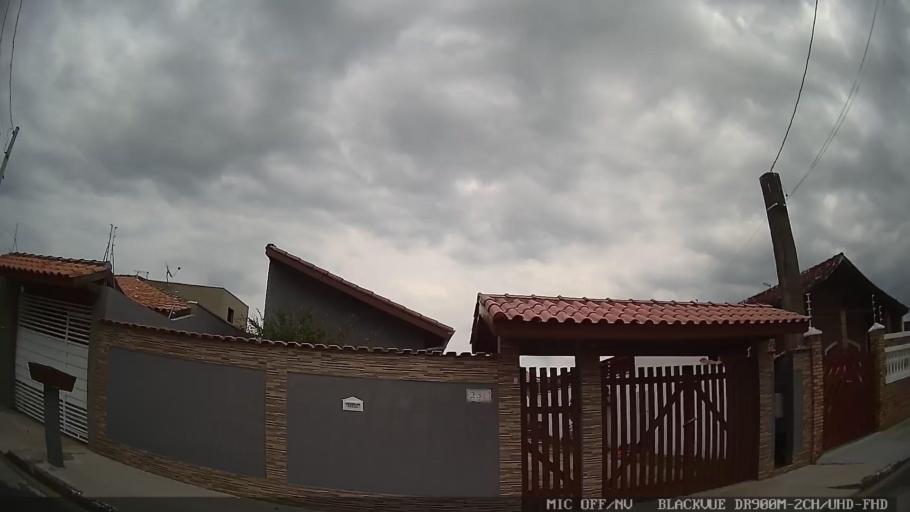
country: BR
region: Sao Paulo
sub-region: Caraguatatuba
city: Caraguatatuba
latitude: -23.6747
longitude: -45.4445
